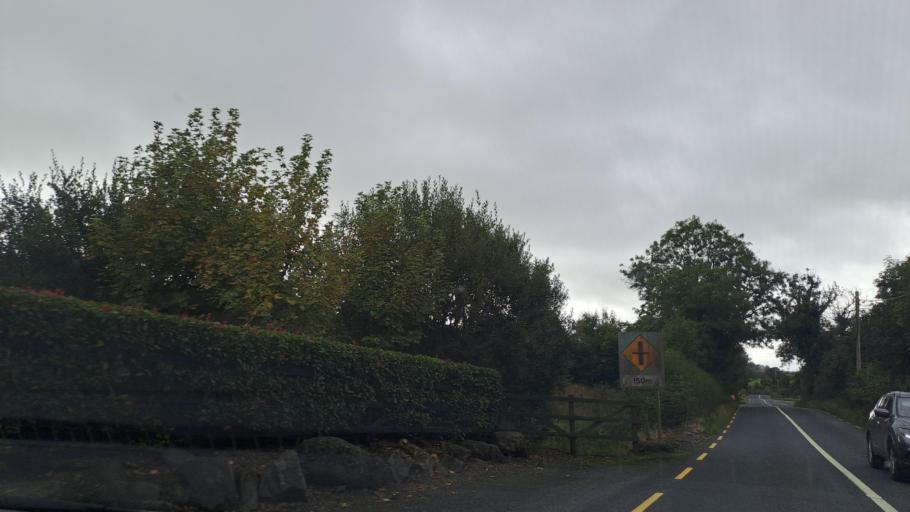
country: IE
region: Ulster
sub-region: An Cabhan
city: Bailieborough
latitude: 53.9408
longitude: -6.9615
